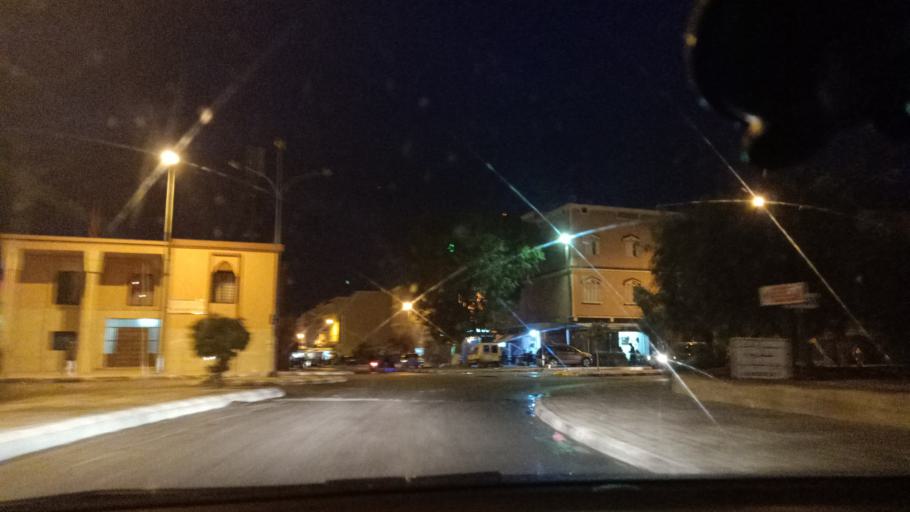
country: MA
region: Doukkala-Abda
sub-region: Safi
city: Youssoufia
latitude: 32.2506
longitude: -8.5338
